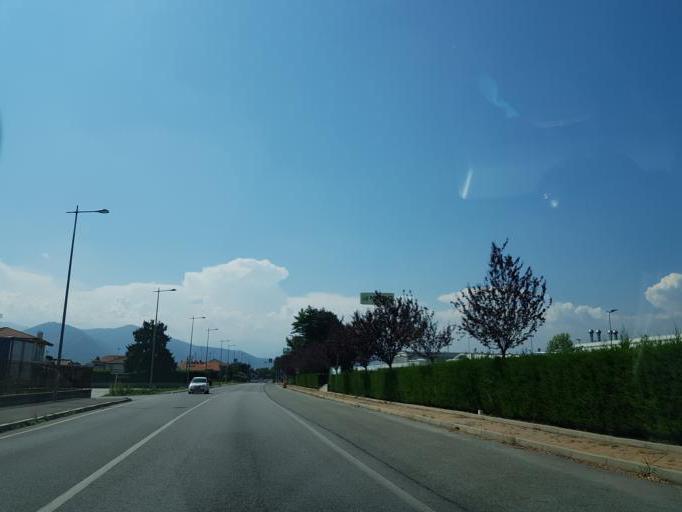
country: IT
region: Piedmont
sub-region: Provincia di Cuneo
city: San Defendente
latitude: 44.3954
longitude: 7.4942
